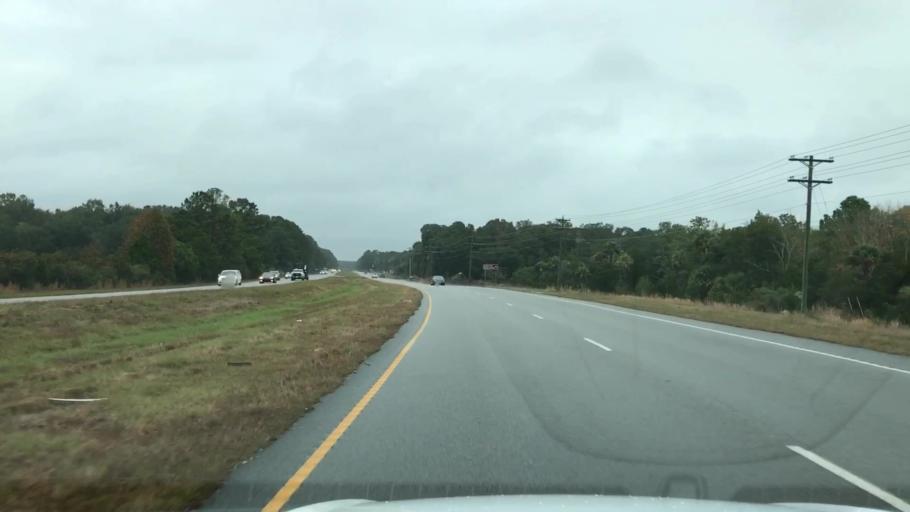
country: US
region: South Carolina
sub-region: Charleston County
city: Isle of Palms
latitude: 32.9193
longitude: -79.7162
